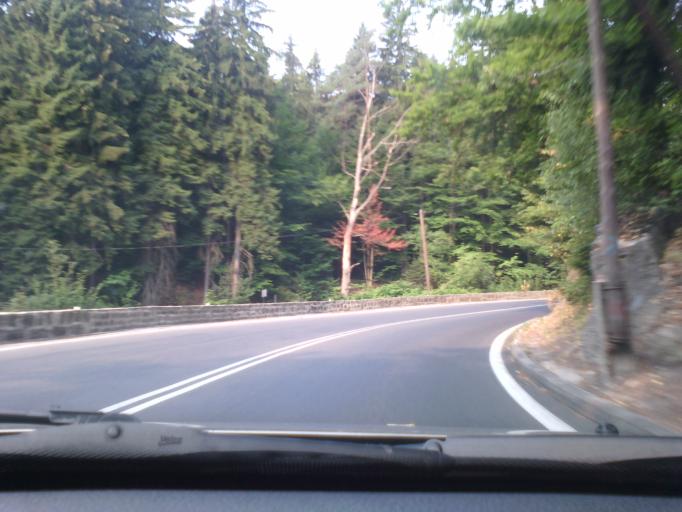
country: PL
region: Lower Silesian Voivodeship
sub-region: Powiat jeleniogorski
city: Szklarska Poreba
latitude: 50.8278
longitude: 15.5394
